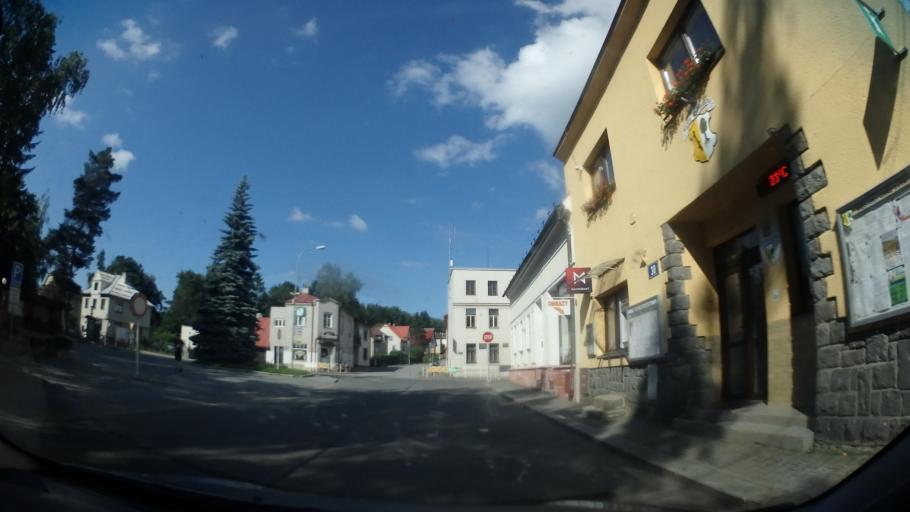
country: CZ
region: Vysocina
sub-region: Okres Zd'ar nad Sazavou
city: Svratka
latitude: 49.7115
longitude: 16.0350
